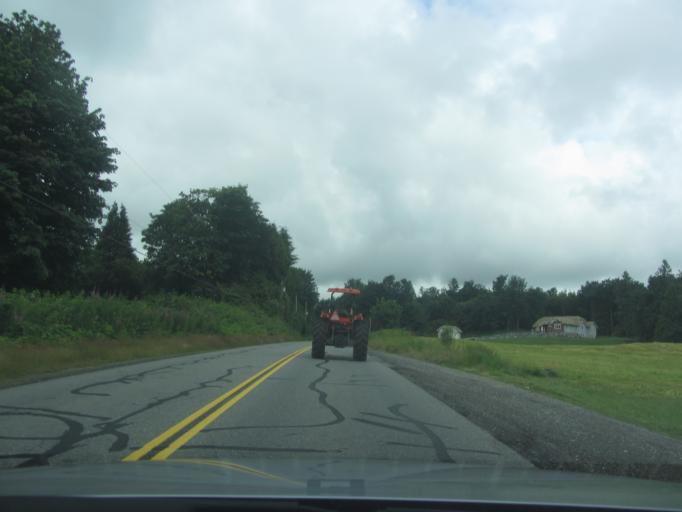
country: CA
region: British Columbia
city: Aldergrove
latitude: 49.1040
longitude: -122.3641
